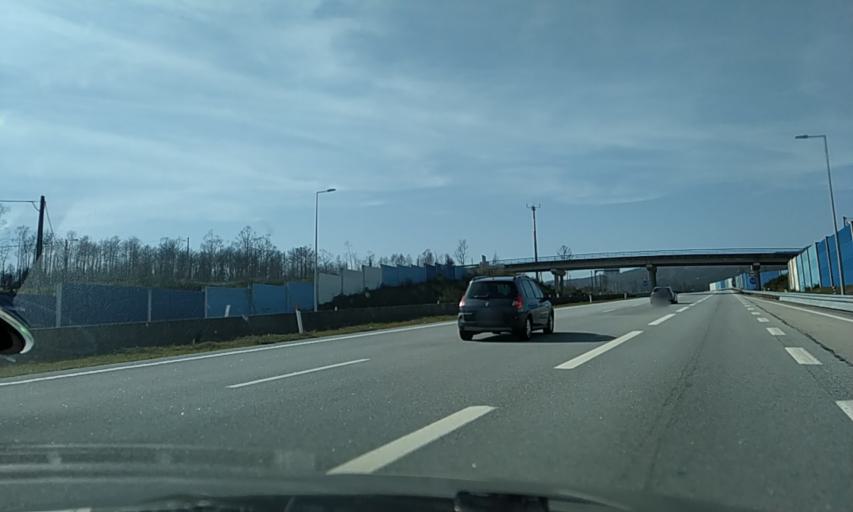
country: PT
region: Viseu
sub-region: Oliveira de Frades
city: Oliveira de Frades
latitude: 40.6878
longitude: -8.2352
